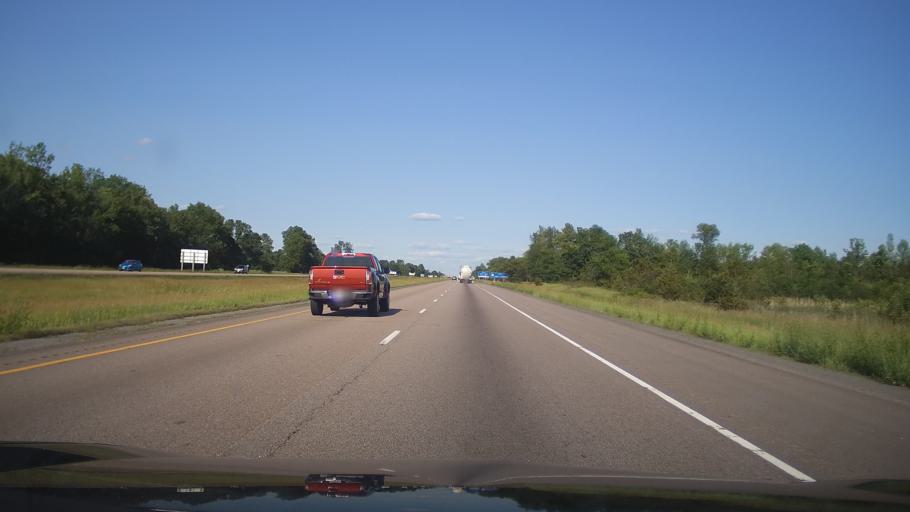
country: CA
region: Ontario
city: Deseronto
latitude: 44.2405
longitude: -77.0906
